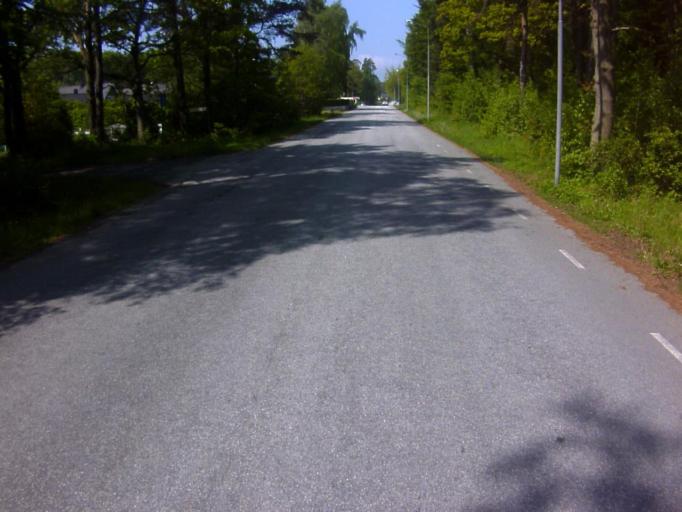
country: SE
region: Blekinge
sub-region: Solvesborgs Kommun
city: Soelvesborg
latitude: 56.0361
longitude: 14.5753
